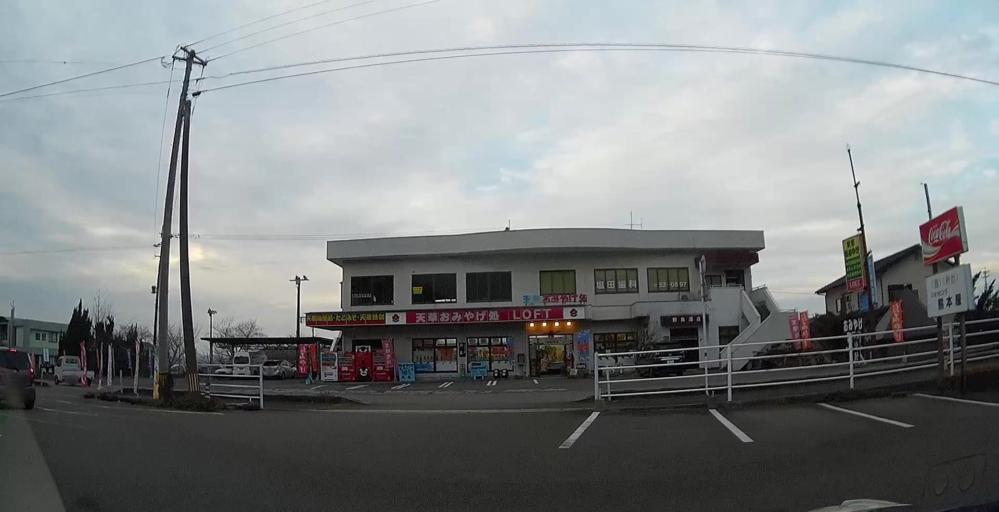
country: JP
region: Kumamoto
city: Hondo
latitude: 32.4732
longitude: 130.2585
